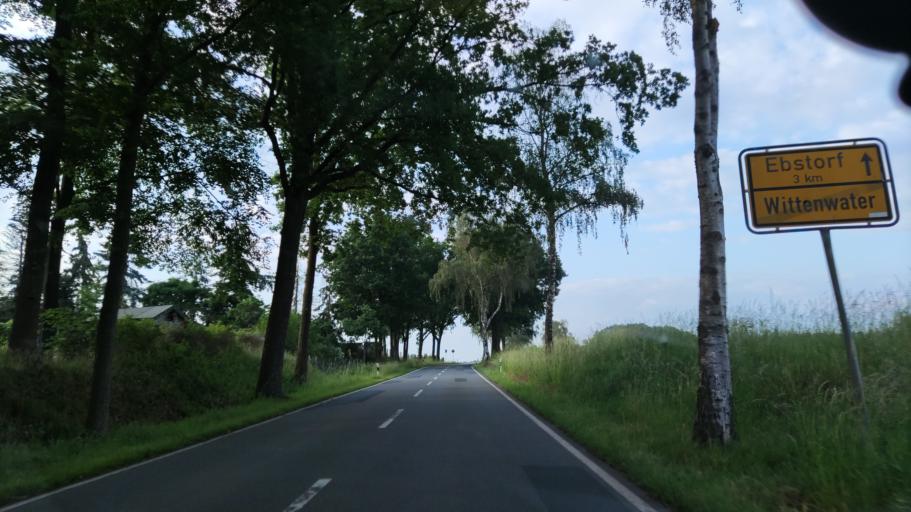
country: DE
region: Lower Saxony
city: Ebstorf
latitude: 53.0035
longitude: 10.4138
